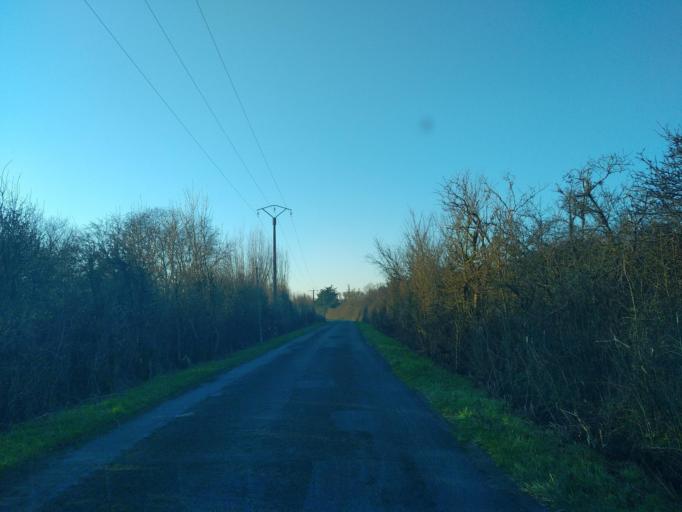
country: FR
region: Pays de la Loire
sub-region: Departement de la Vendee
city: Triaize
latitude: 46.3910
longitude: -1.2840
